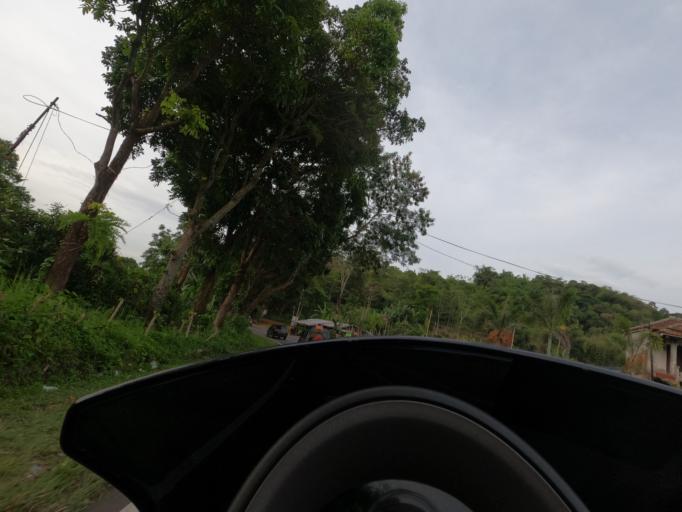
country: ID
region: West Java
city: Lembang
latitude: -6.7221
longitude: 107.6623
